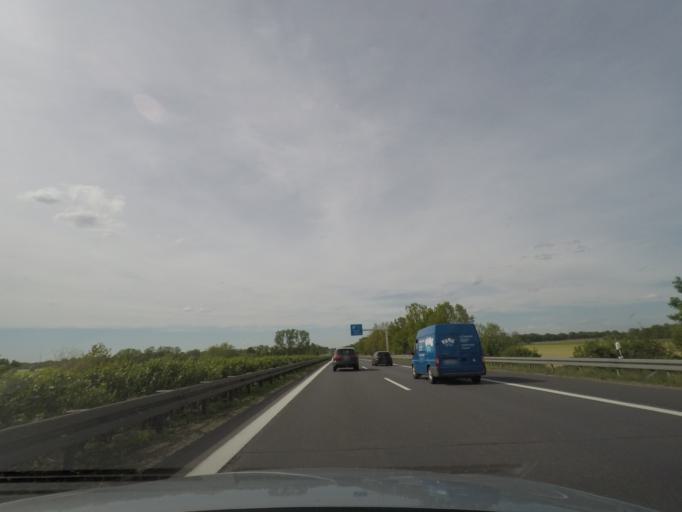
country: DE
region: Brandenburg
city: Mittenwalde
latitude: 52.2819
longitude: 13.5663
